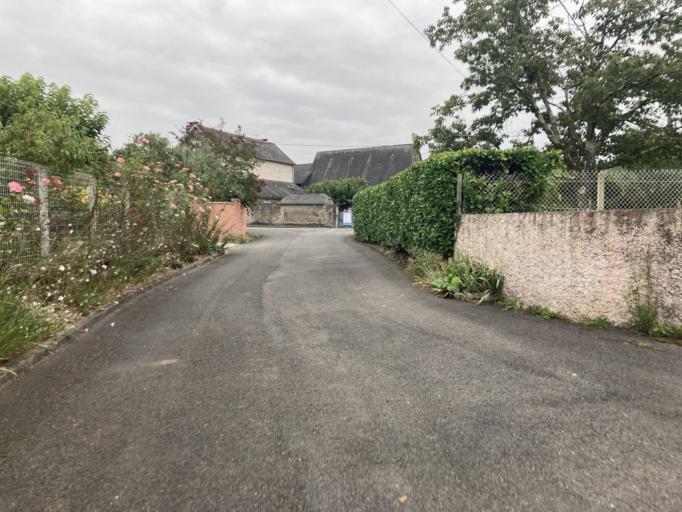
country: FR
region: Aquitaine
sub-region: Departement des Pyrenees-Atlantiques
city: Artiguelouve
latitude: 43.3248
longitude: -0.4813
